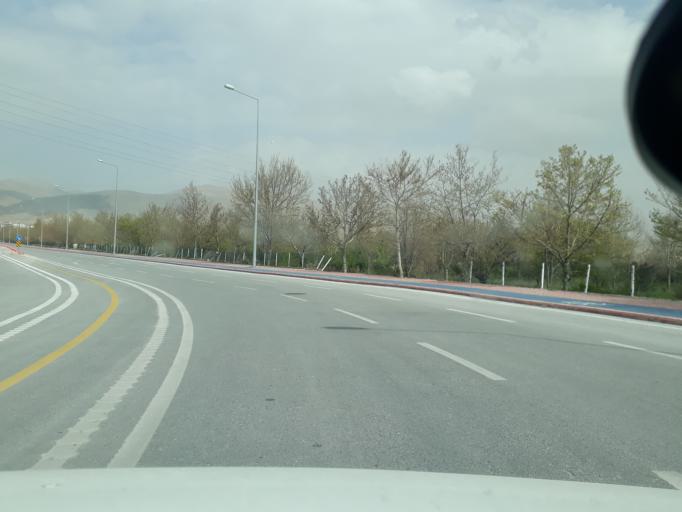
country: TR
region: Konya
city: Selcuklu
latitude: 37.9463
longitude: 32.4803
